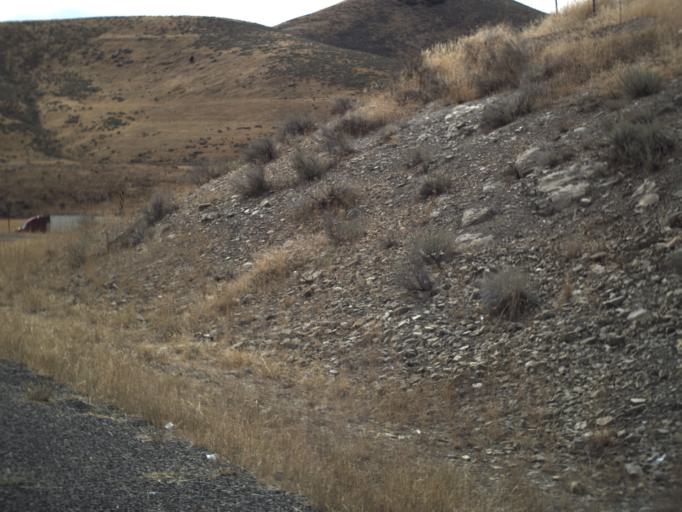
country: US
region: Utah
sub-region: Box Elder County
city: Garland
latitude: 41.8010
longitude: -112.3038
